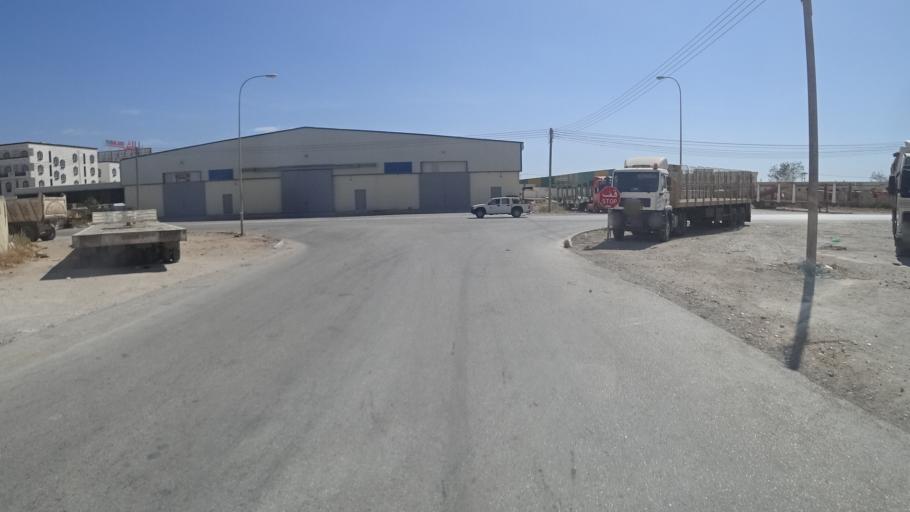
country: OM
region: Zufar
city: Salalah
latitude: 17.0312
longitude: 54.0511
